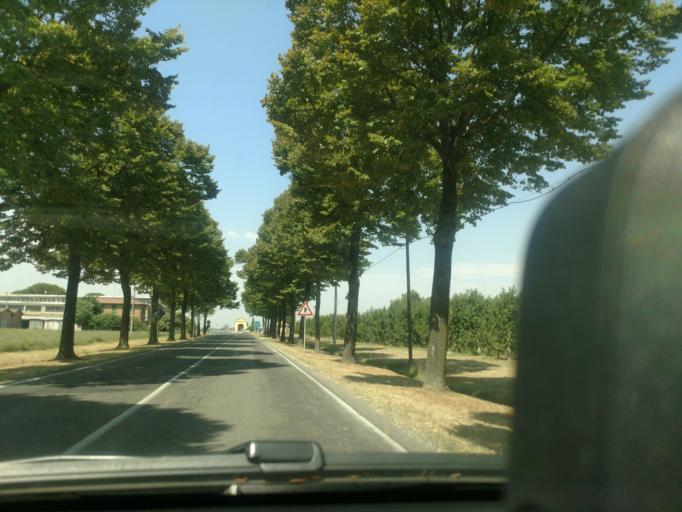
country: IT
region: Emilia-Romagna
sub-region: Provincia di Bologna
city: Castel Guelfo di Bologna
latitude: 44.4363
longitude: 11.6590
